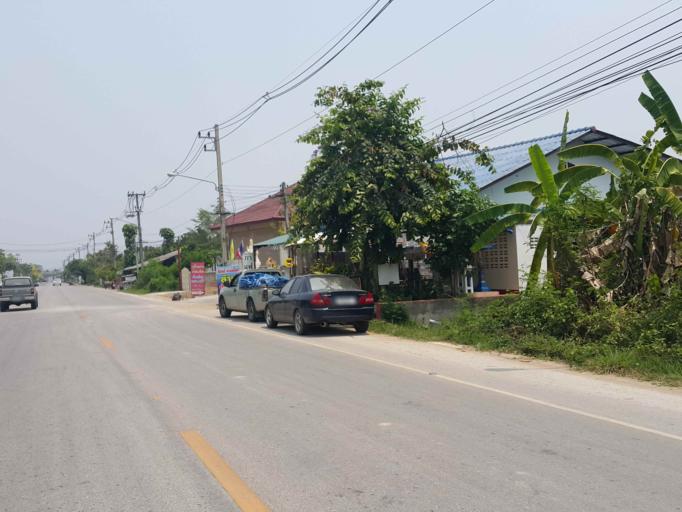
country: TH
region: Chiang Mai
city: San Sai
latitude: 18.8307
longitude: 99.1280
